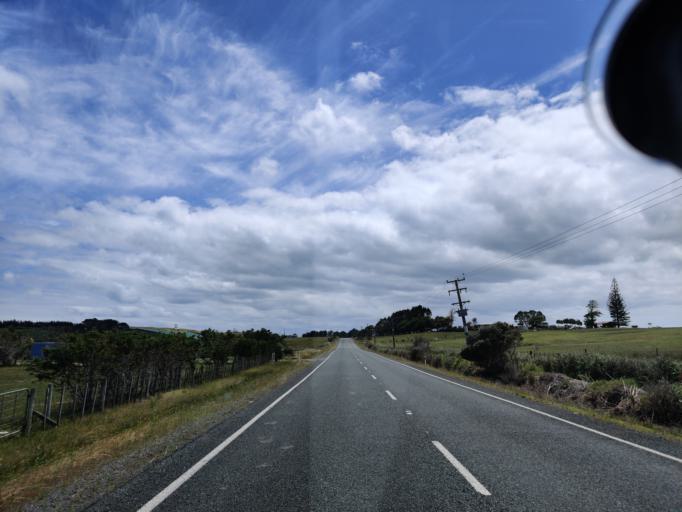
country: NZ
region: Northland
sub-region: Far North District
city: Kaitaia
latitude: -34.7331
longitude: 173.0454
